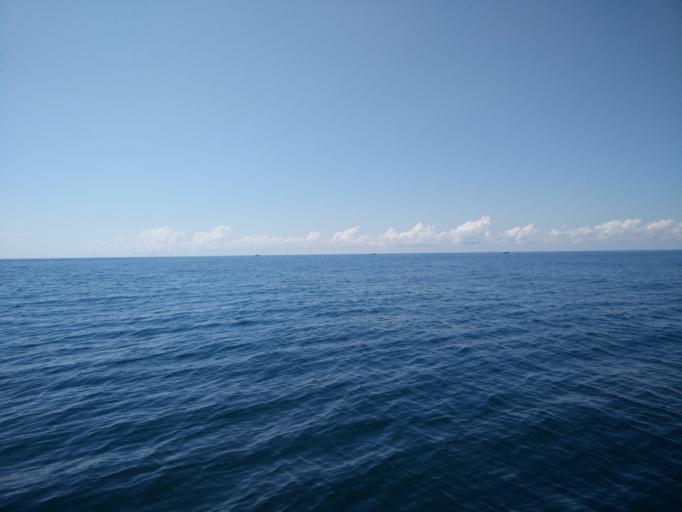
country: MM
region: Ayeyarwady
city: Pathein
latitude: 16.8567
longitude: 94.2712
